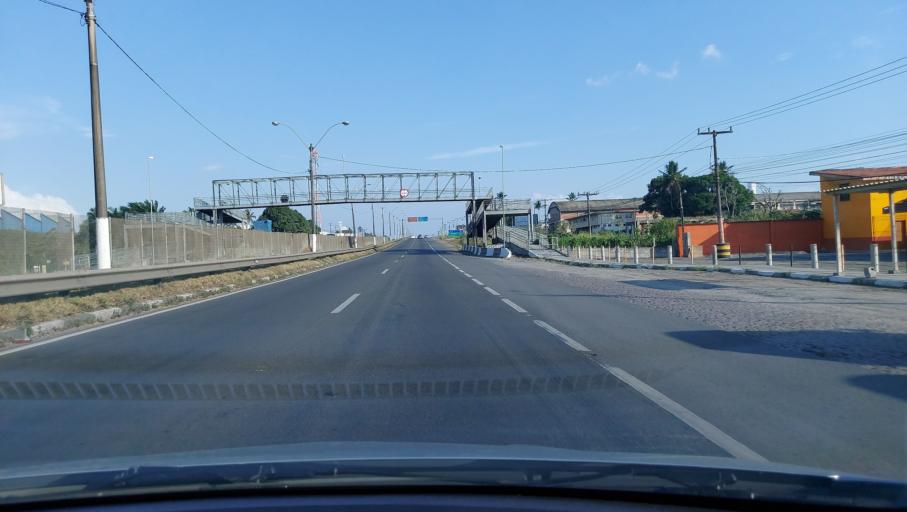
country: BR
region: Bahia
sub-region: Feira De Santana
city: Feira de Santana
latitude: -12.2787
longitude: -38.9267
